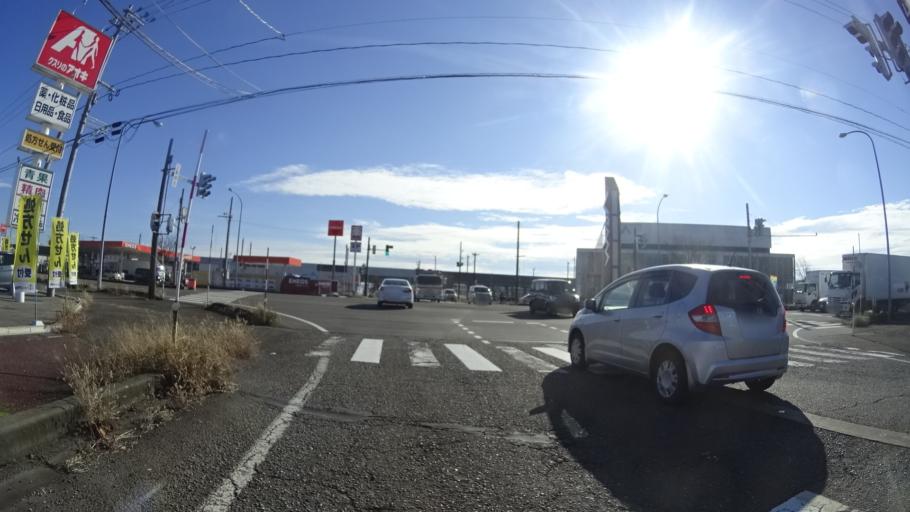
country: JP
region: Niigata
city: Mitsuke
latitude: 37.5420
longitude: 138.8896
